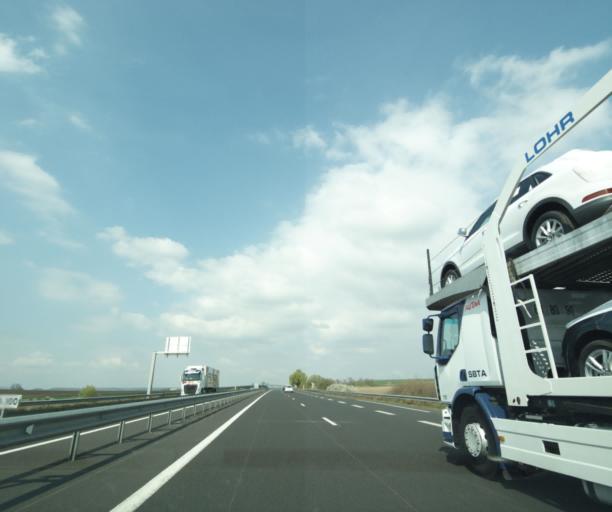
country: FR
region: Auvergne
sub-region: Departement du Puy-de-Dome
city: Le Breuil-sur-Couze
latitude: 45.4261
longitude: 3.2729
